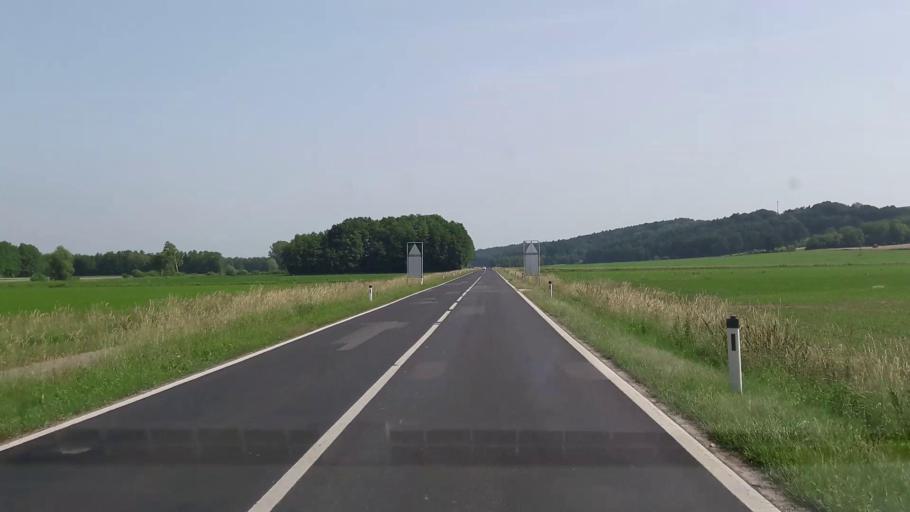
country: AT
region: Burgenland
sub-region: Politischer Bezirk Jennersdorf
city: Deutsch Kaltenbrunn
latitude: 47.0961
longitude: 16.1067
